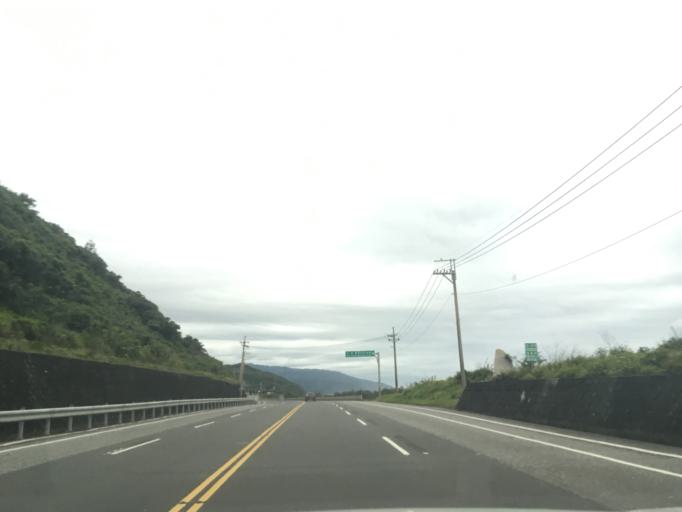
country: TW
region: Taiwan
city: Hengchun
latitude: 22.2964
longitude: 120.8886
